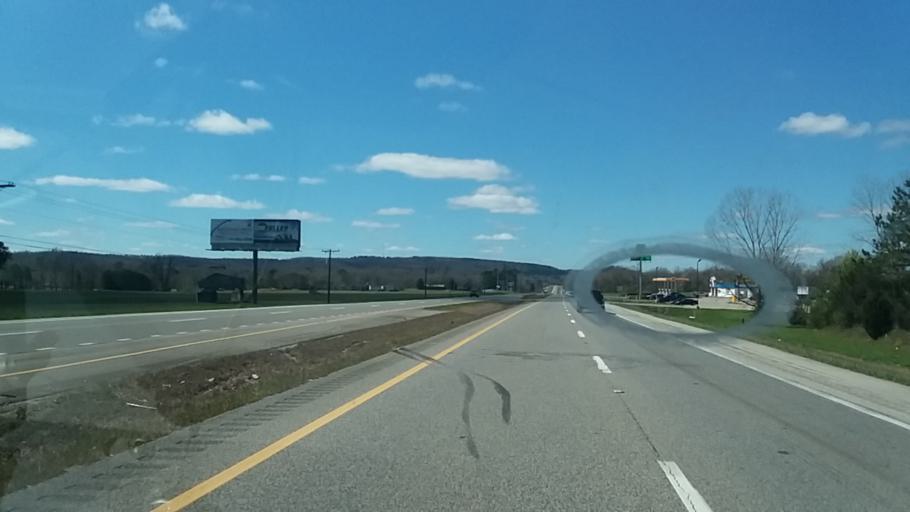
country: US
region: Alabama
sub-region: Colbert County
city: Tuscumbia
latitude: 34.7095
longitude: -87.7417
